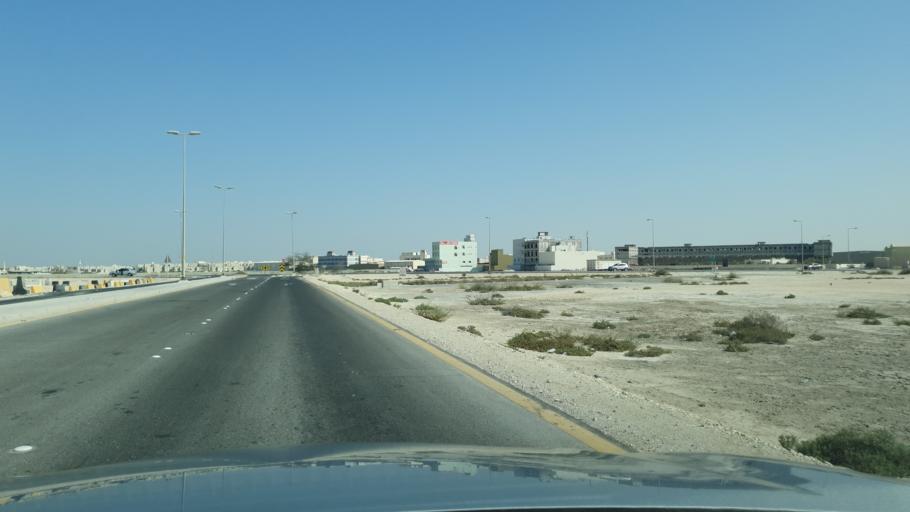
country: BH
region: Northern
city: Madinat `Isa
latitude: 26.1823
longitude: 50.5057
